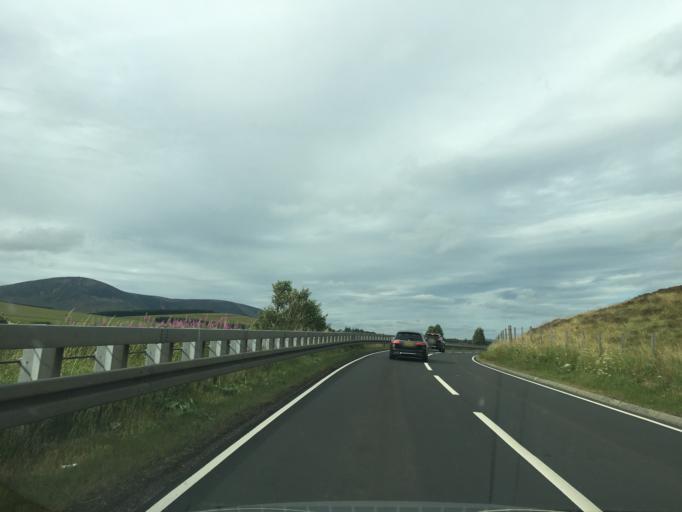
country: GB
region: Scotland
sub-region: South Lanarkshire
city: Biggar
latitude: 55.5416
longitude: -3.6587
